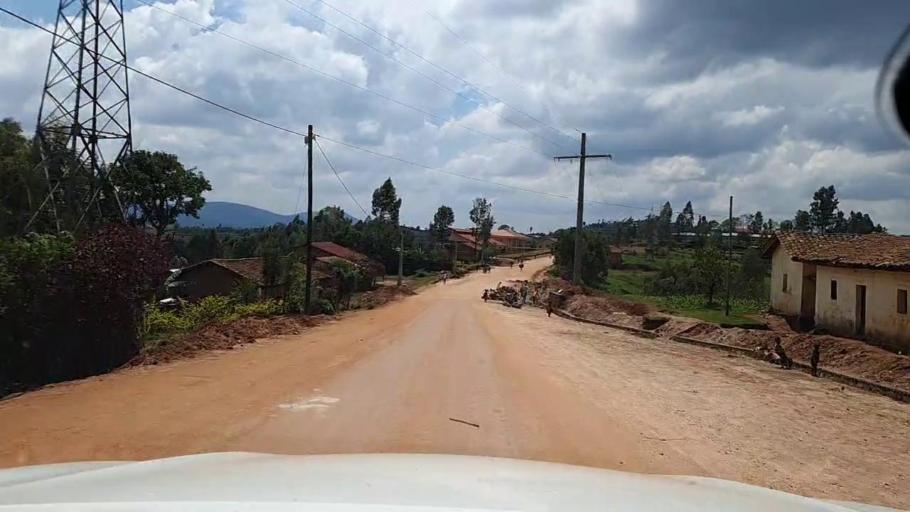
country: RW
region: Southern Province
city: Butare
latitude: -2.6904
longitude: 29.5670
